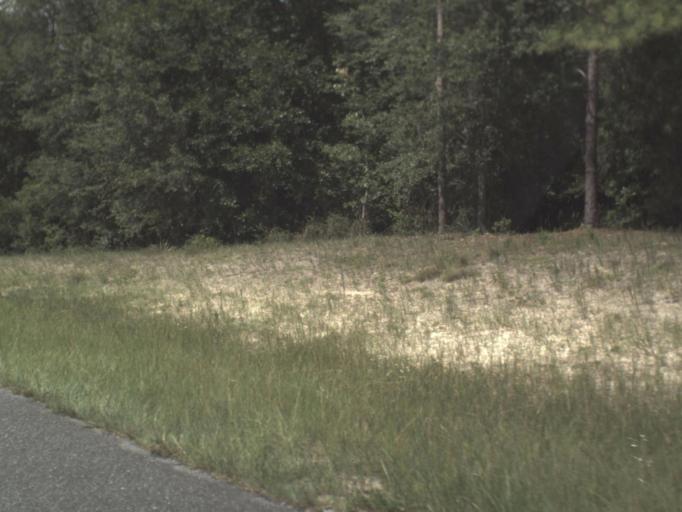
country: US
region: Florida
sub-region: Alachua County
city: High Springs
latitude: 29.7622
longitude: -82.7406
